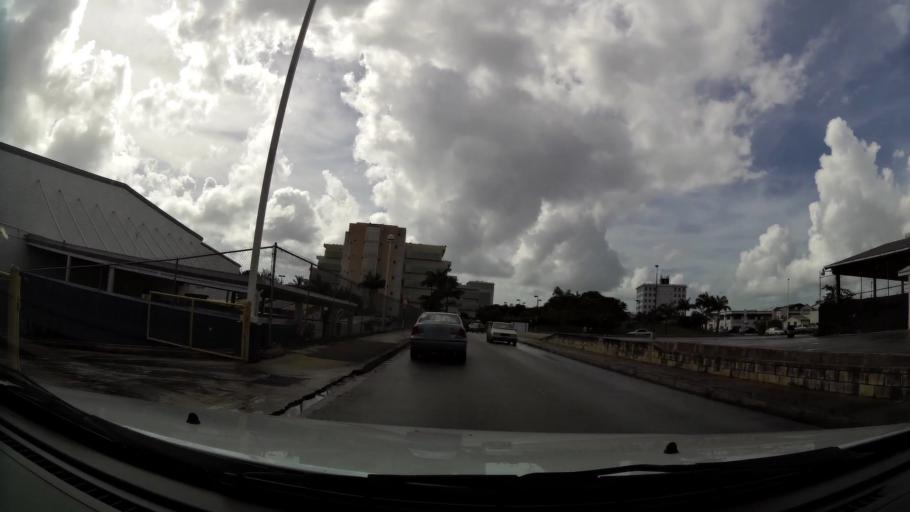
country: BB
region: Saint Michael
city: Bridgetown
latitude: 13.1403
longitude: -59.6073
